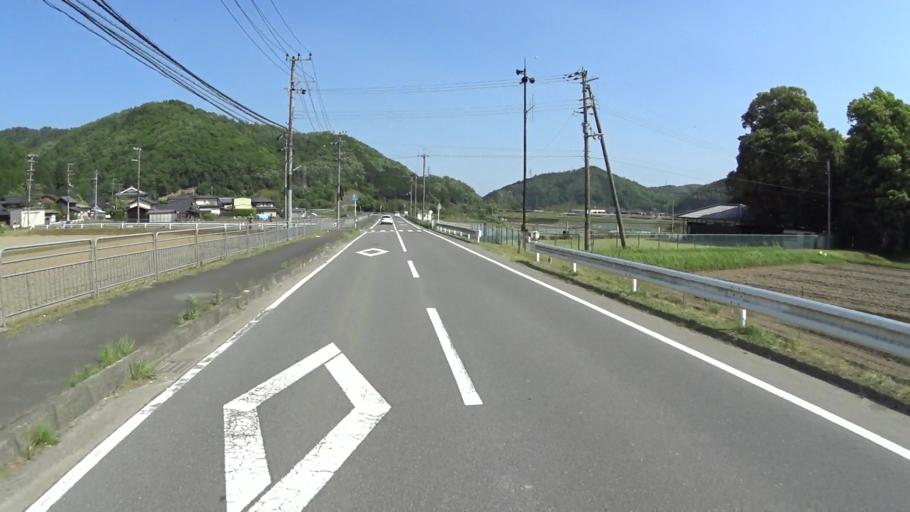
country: JP
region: Kyoto
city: Kameoka
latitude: 35.1267
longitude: 135.4997
